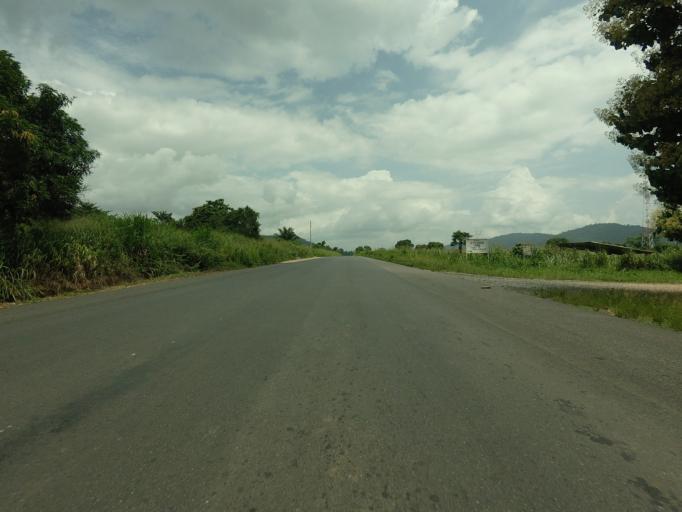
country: GH
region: Volta
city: Ho
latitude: 6.5551
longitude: 0.2592
